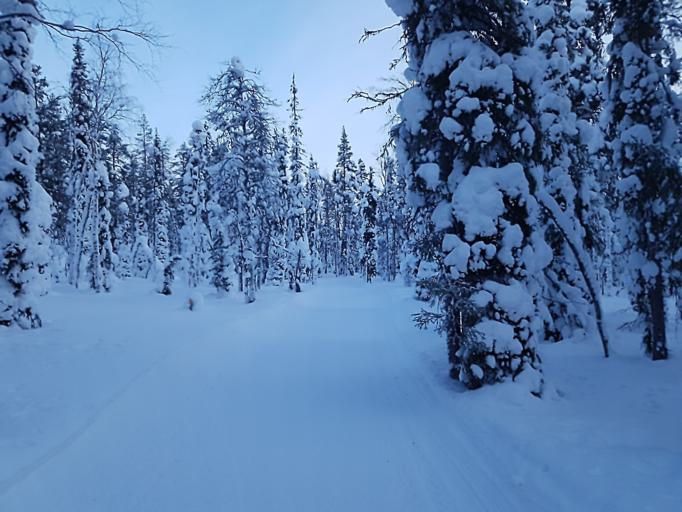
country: FI
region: Lapland
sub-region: Tunturi-Lappi
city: Kolari
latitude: 67.6378
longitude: 24.2293
